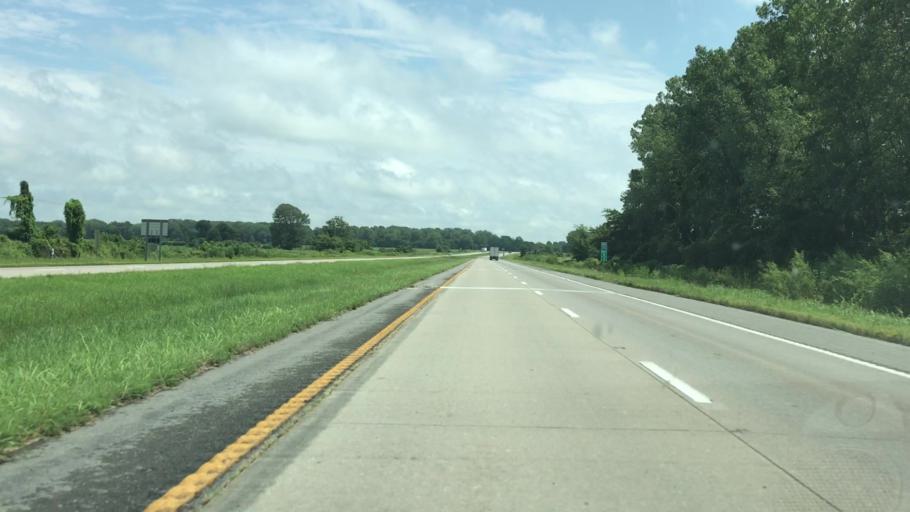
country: US
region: Missouri
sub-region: Pemiscot County
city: Caruthersville
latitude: 36.1407
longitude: -89.6391
